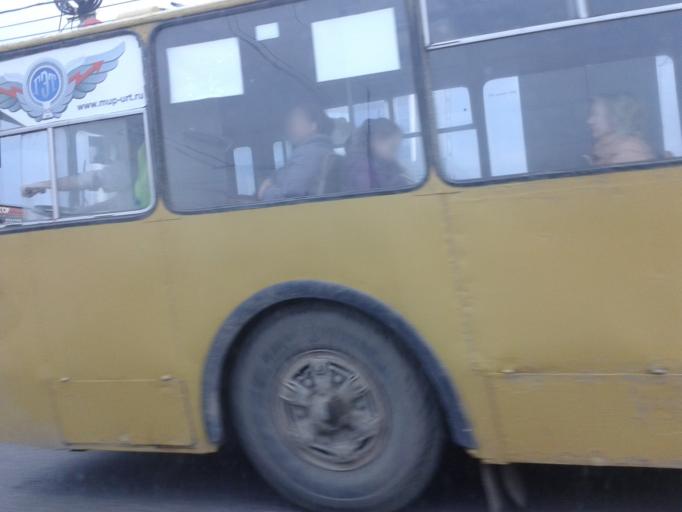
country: RU
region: Rjazan
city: Ryazan'
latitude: 54.6334
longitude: 39.6967
